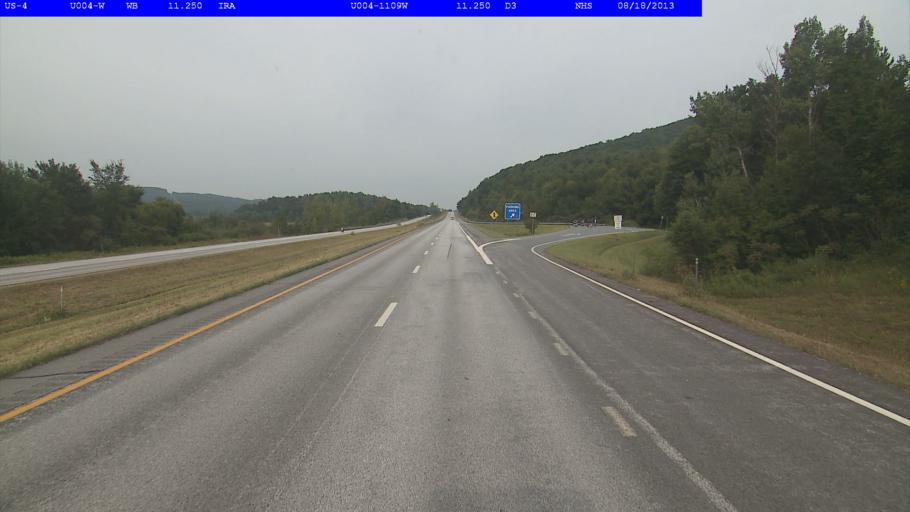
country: US
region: Vermont
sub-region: Rutland County
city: West Rutland
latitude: 43.6135
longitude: -73.0970
